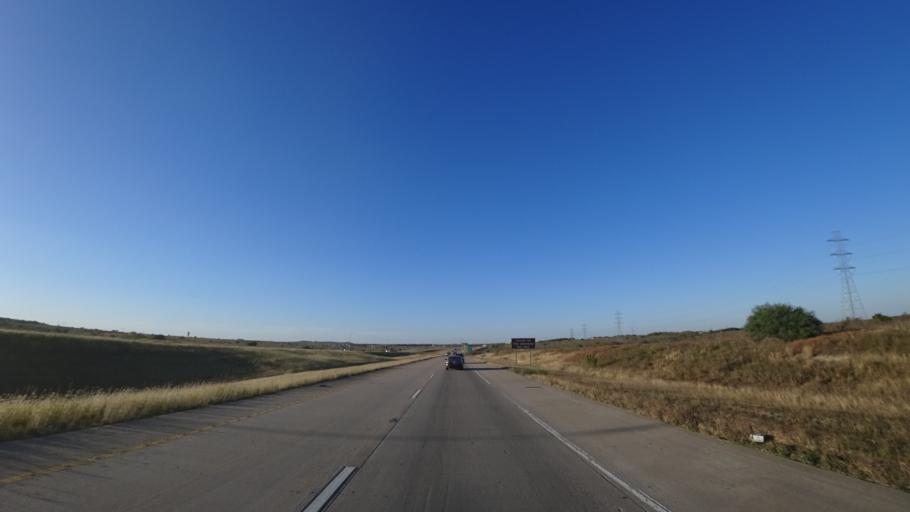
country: US
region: Texas
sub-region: Travis County
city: Garfield
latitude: 30.1266
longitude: -97.6624
